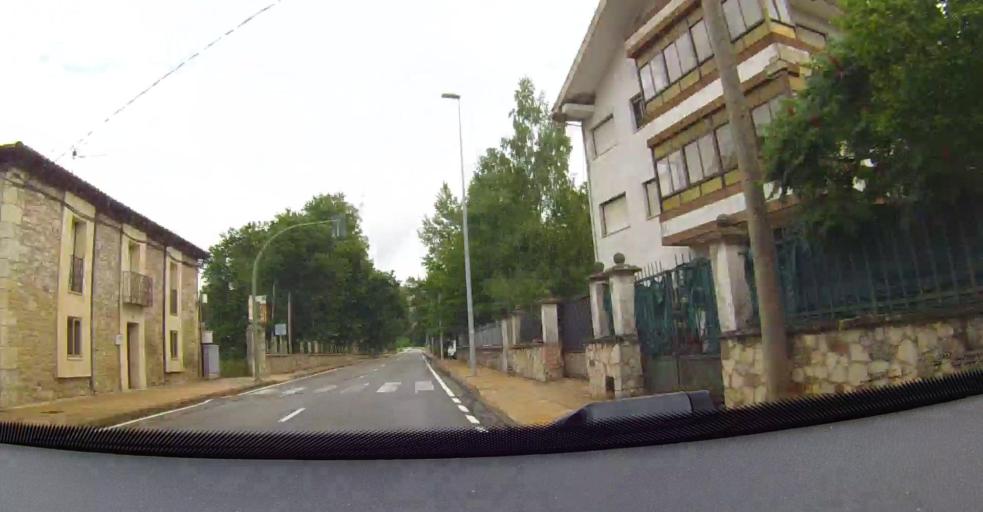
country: ES
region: Castille and Leon
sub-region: Provincia de Leon
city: Bonar
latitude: 42.8768
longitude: -5.3197
